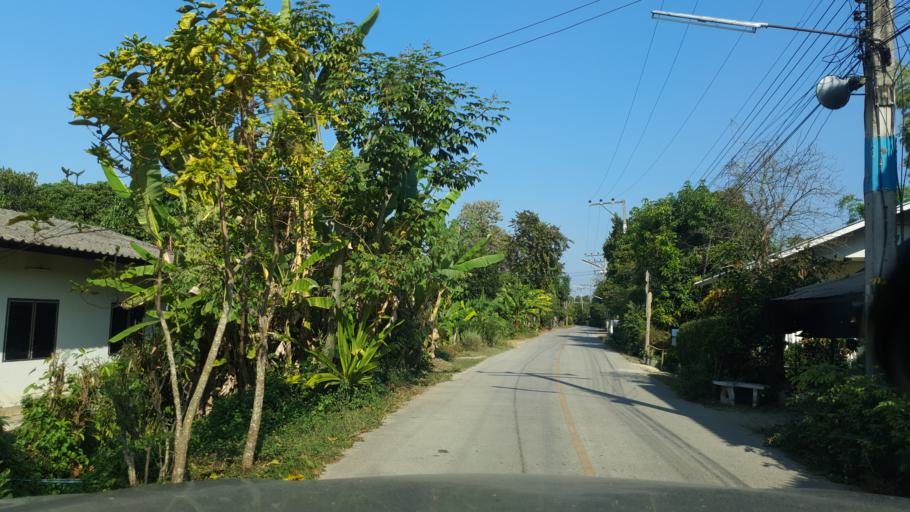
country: TH
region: Chiang Mai
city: Saraphi
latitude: 18.7092
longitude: 99.0745
